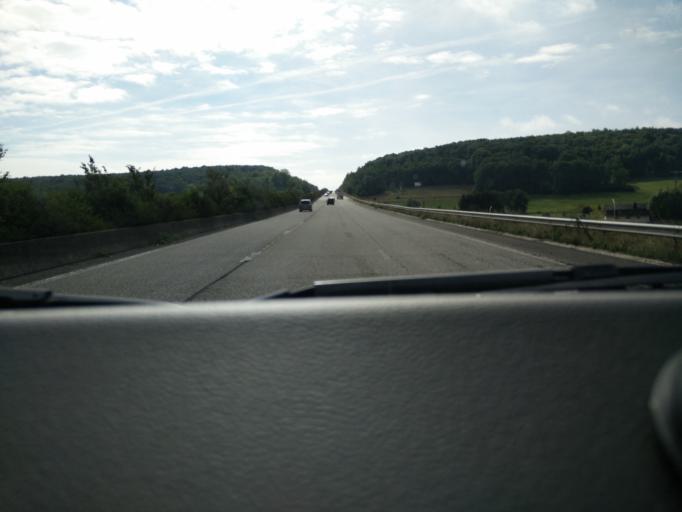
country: BE
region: Wallonia
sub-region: Province du Luxembourg
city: Wellin
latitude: 50.1177
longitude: 5.1024
